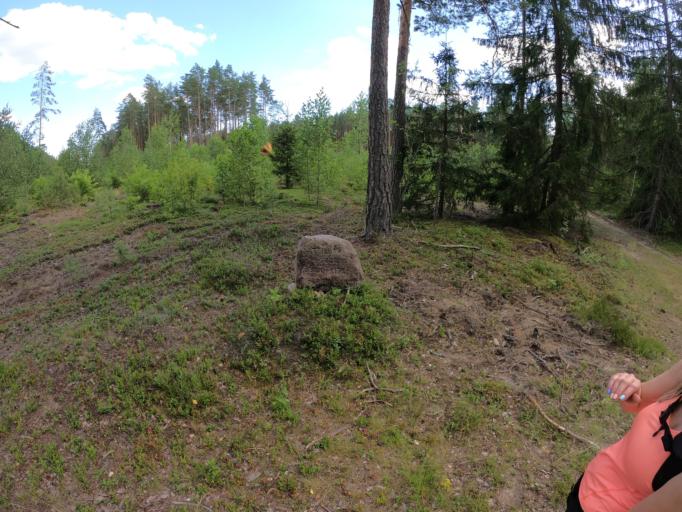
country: LT
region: Alytaus apskritis
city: Druskininkai
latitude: 54.0195
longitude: 23.8289
